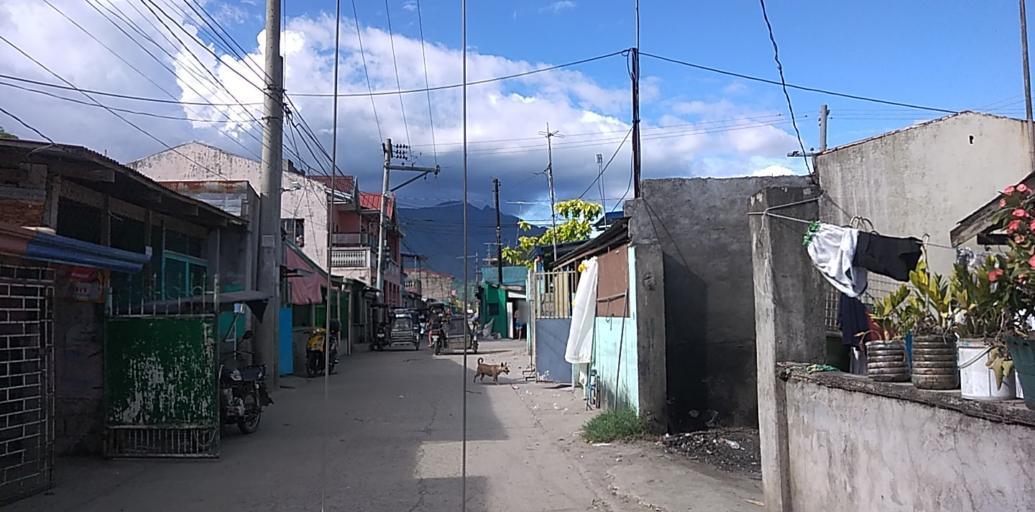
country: PH
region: Central Luzon
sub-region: Province of Pampanga
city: Arayat
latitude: 15.1384
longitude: 120.7702
